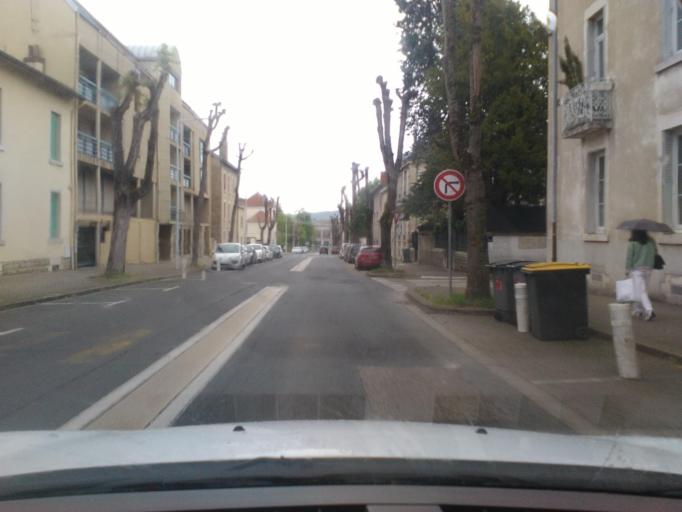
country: FR
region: Rhone-Alpes
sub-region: Departement de l'Ain
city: Bourg-en-Bresse
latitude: 46.2006
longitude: 5.2210
